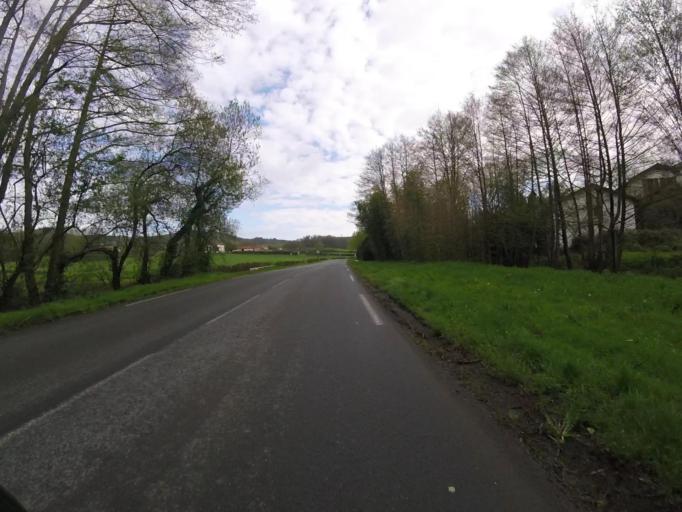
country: FR
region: Aquitaine
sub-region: Departement des Pyrenees-Atlantiques
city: Sare
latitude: 43.3133
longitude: -1.5842
